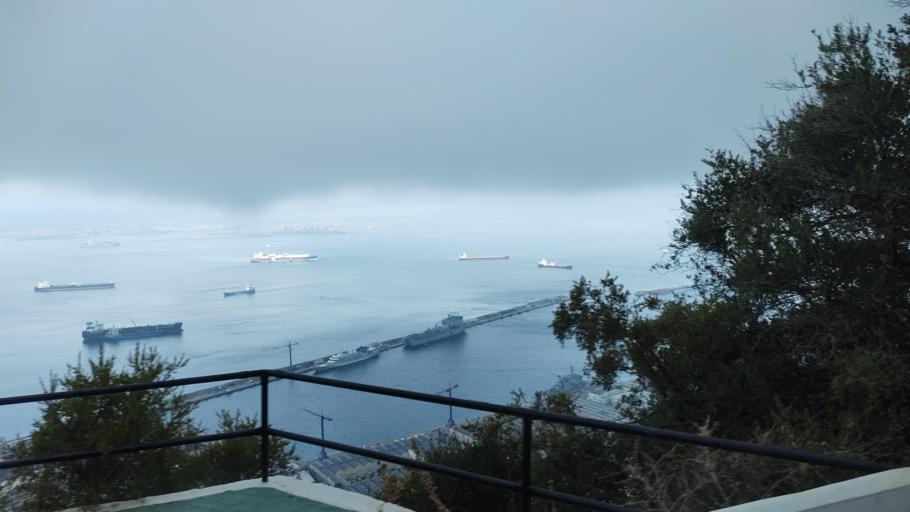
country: GI
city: Gibraltar
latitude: 36.1276
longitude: -5.3469
